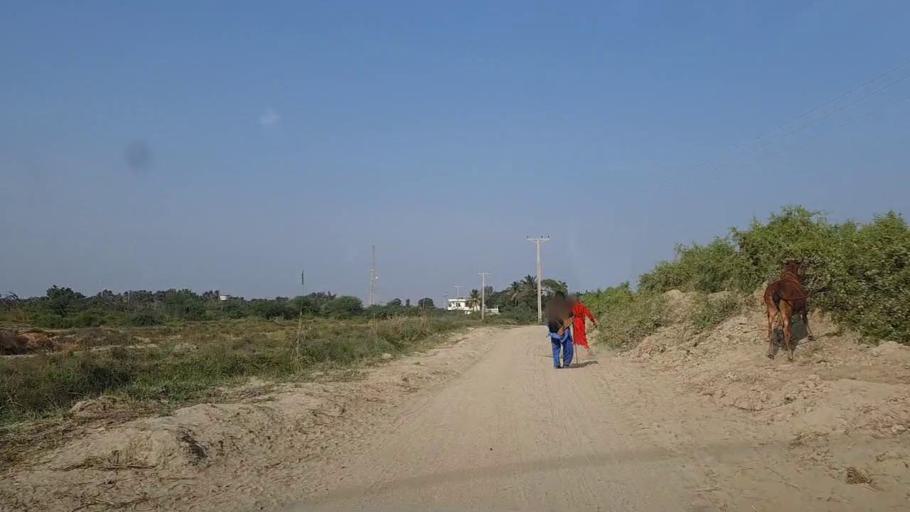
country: PK
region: Sindh
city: Mirpur Sakro
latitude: 24.5881
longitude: 67.5686
